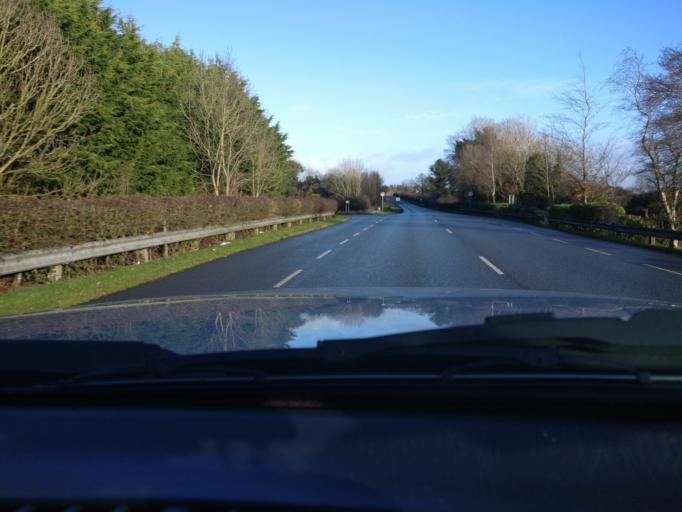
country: IE
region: Leinster
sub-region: An Iarmhi
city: An Muileann gCearr
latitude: 53.5085
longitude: -7.4150
